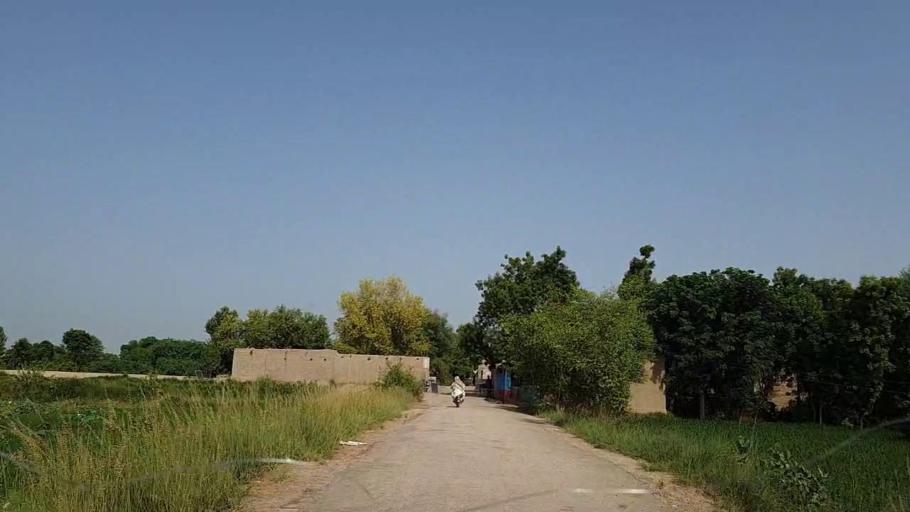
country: PK
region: Sindh
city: Kandiaro
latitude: 27.0707
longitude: 68.1619
